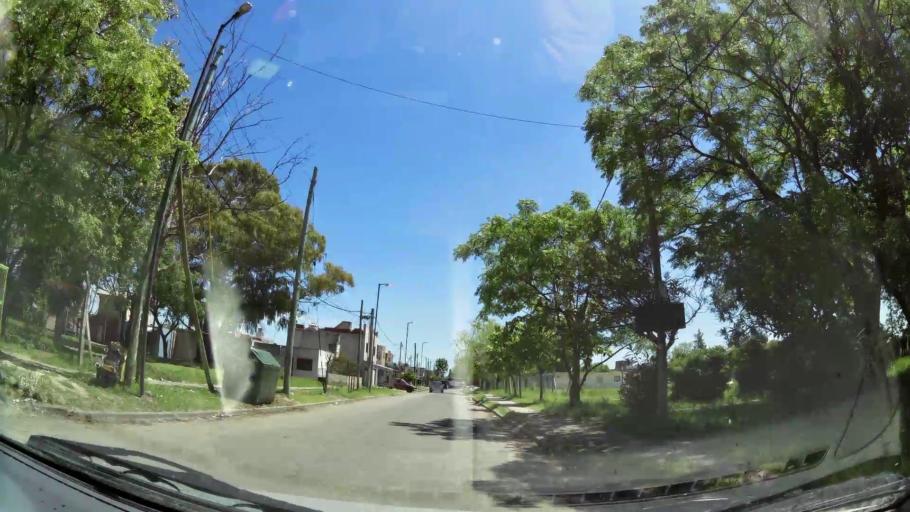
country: AR
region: Buenos Aires
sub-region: Partido de Quilmes
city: Quilmes
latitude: -34.7139
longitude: -58.3135
